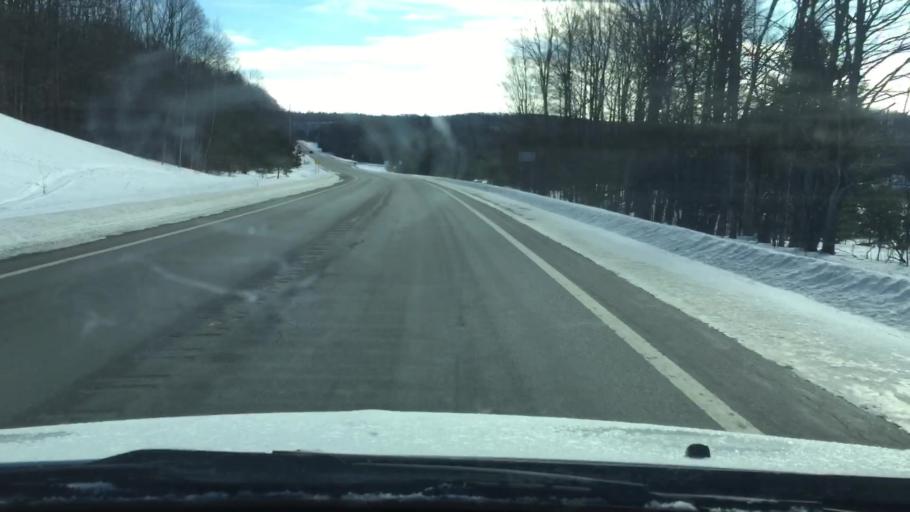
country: US
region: Michigan
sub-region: Antrim County
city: Mancelona
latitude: 44.9706
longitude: -85.0548
